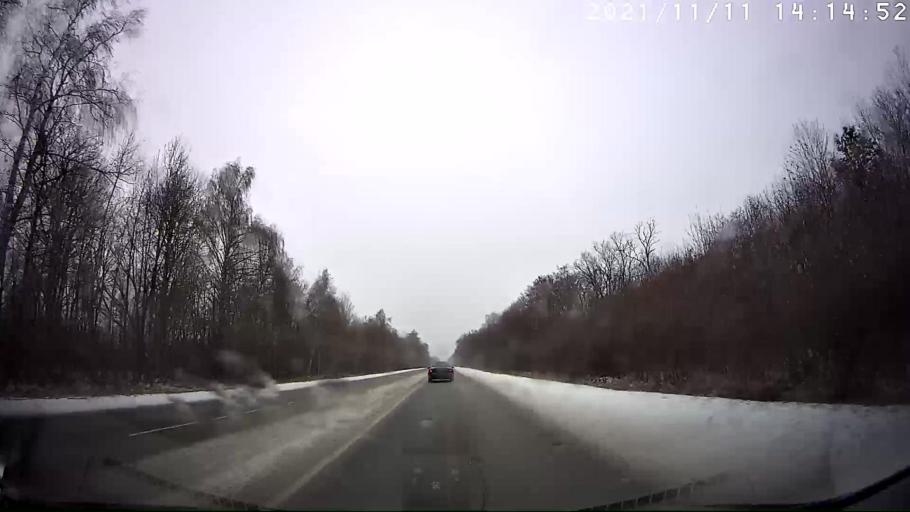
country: RU
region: Chuvashia
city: Tsivil'sk
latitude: 55.8280
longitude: 47.4520
